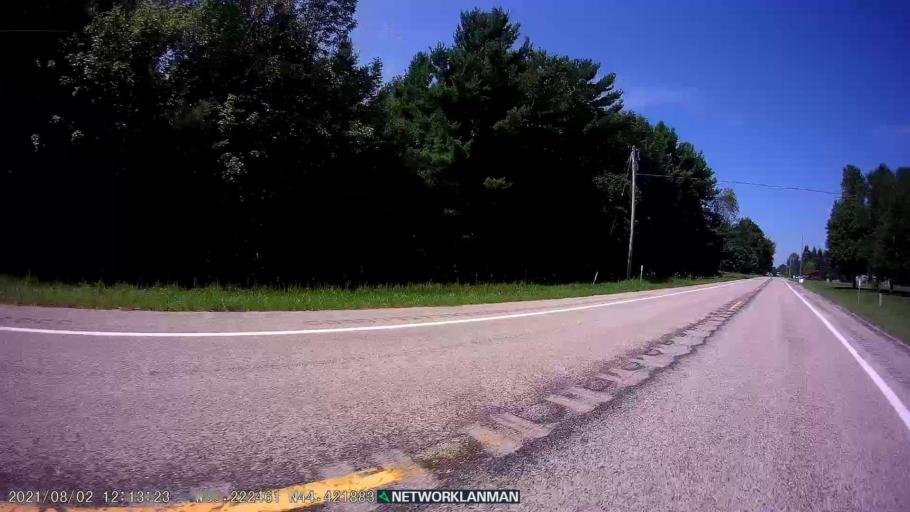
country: US
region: Michigan
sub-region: Manistee County
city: Manistee
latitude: 44.4221
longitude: -86.2225
